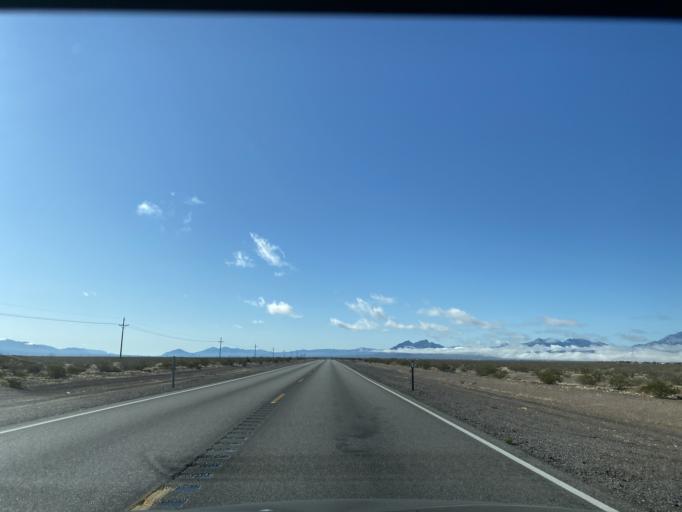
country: US
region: Nevada
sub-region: Nye County
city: Beatty
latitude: 36.5646
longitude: -116.4144
